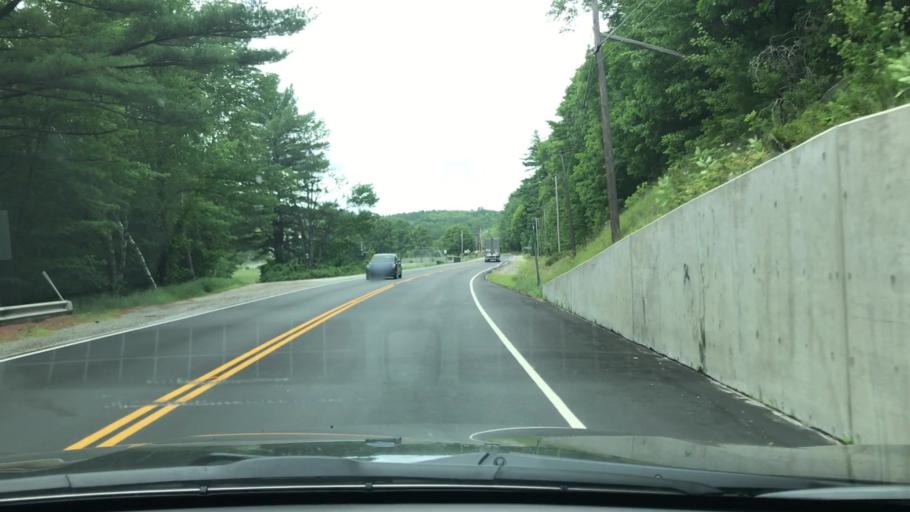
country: US
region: Maine
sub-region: Oxford County
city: West Paris
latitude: 44.3830
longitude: -70.6521
